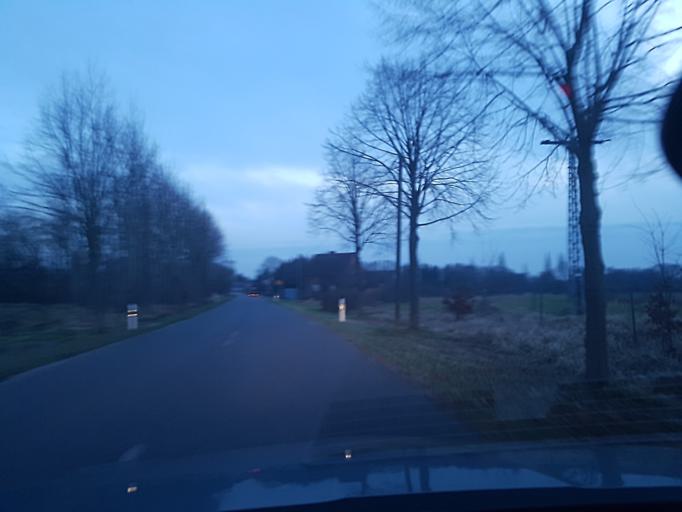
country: DE
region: Brandenburg
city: Ruckersdorf
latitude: 51.5995
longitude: 13.5467
